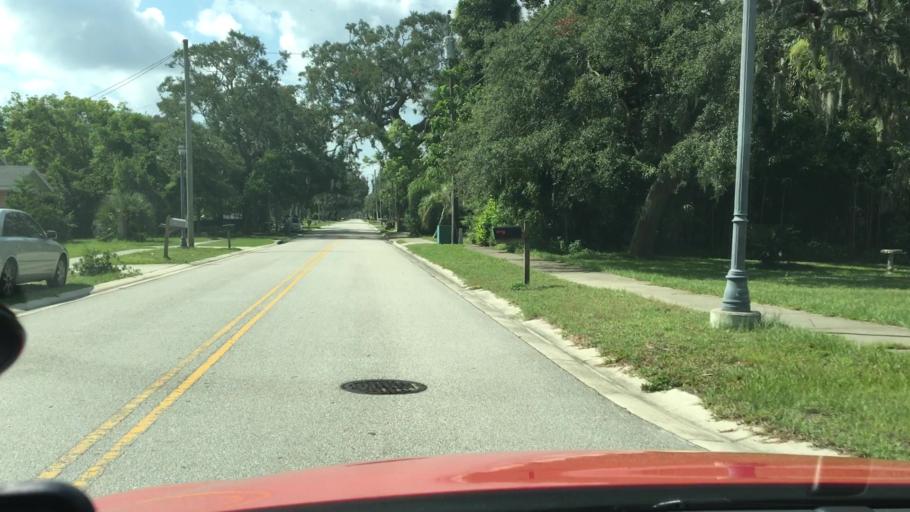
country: US
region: Florida
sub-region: Volusia County
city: Ormond Beach
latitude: 29.2814
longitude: -81.0573
